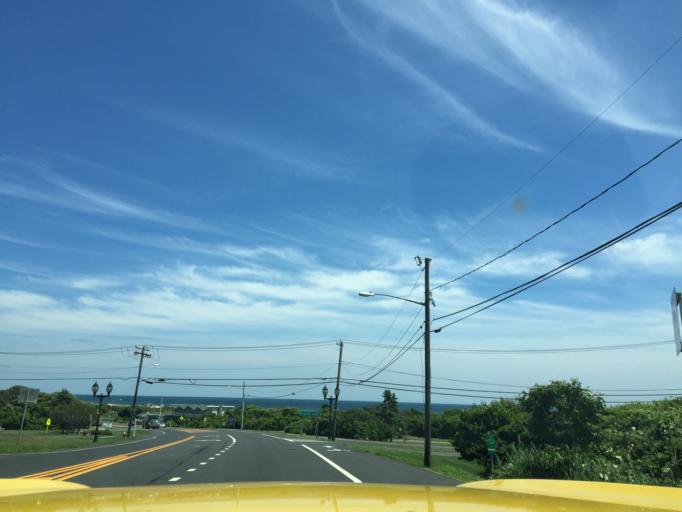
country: US
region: New York
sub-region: Suffolk County
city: Montauk
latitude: 41.0311
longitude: -71.9554
